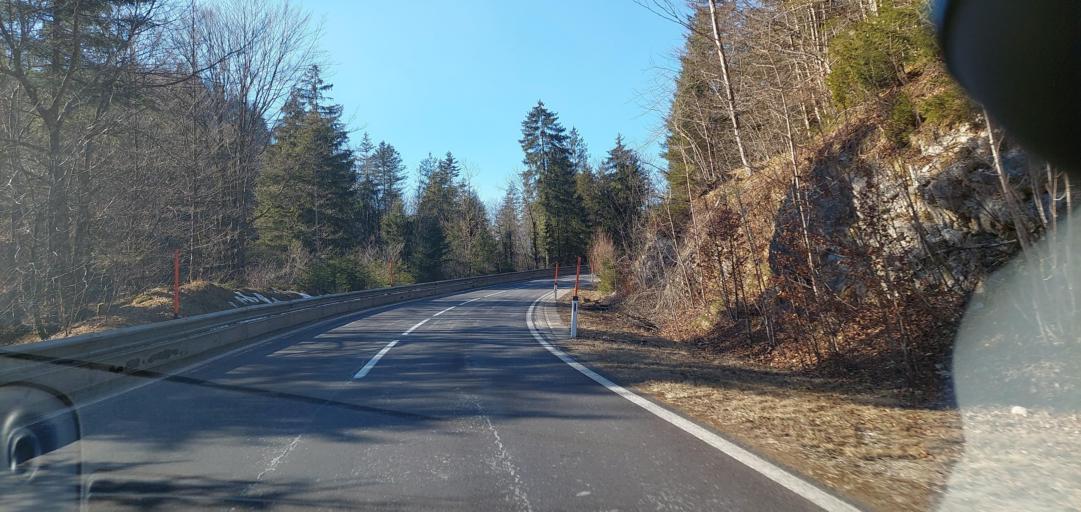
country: AT
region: Upper Austria
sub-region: Politischer Bezirk Gmunden
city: Bad Ischl
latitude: 47.7634
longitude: 13.6476
